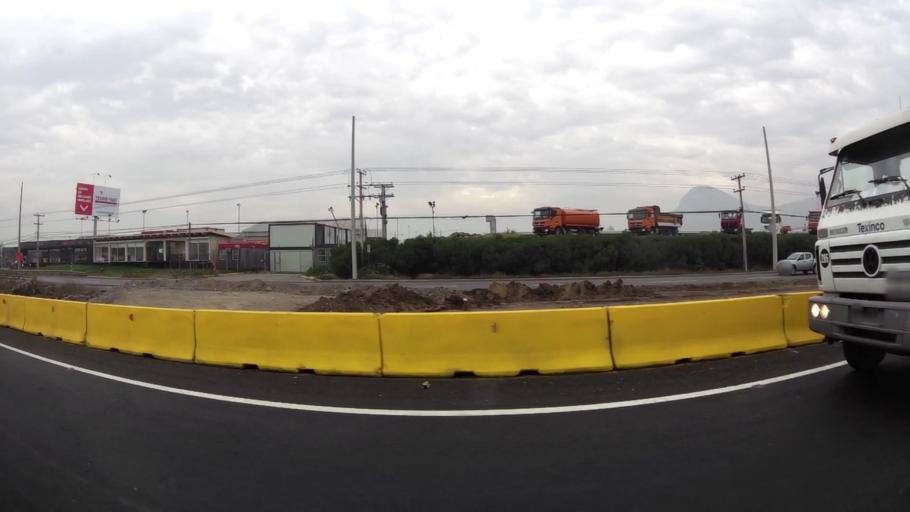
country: CL
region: Santiago Metropolitan
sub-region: Provincia de Chacabuco
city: Chicureo Abajo
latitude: -33.3096
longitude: -70.7255
